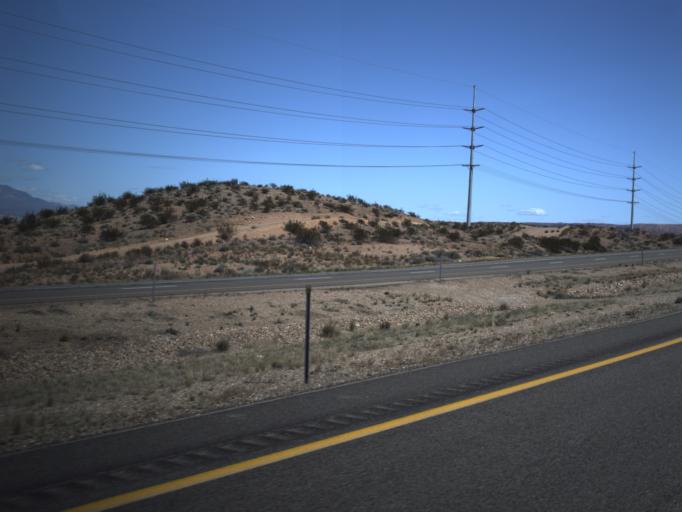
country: US
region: Utah
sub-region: Washington County
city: Saint George
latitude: 37.0051
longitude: -113.5252
